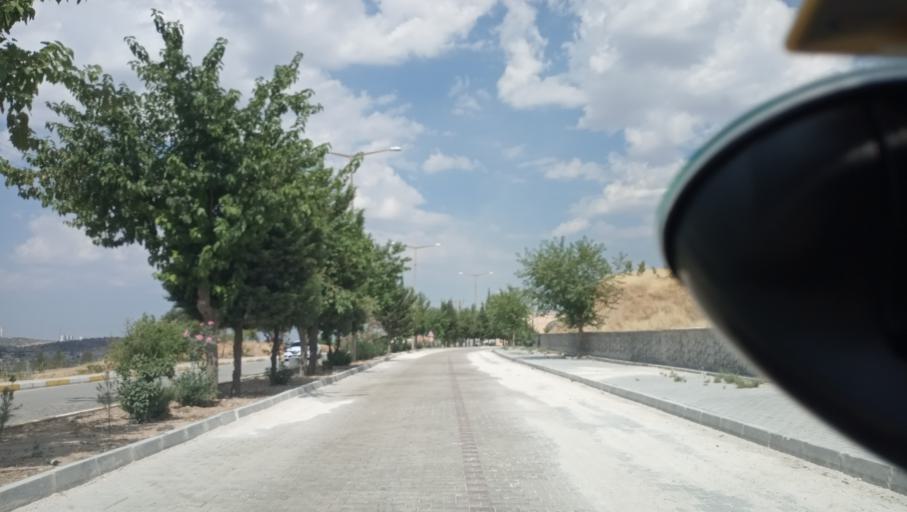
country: TR
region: Mardin
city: Kabala
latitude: 37.3424
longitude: 40.8071
